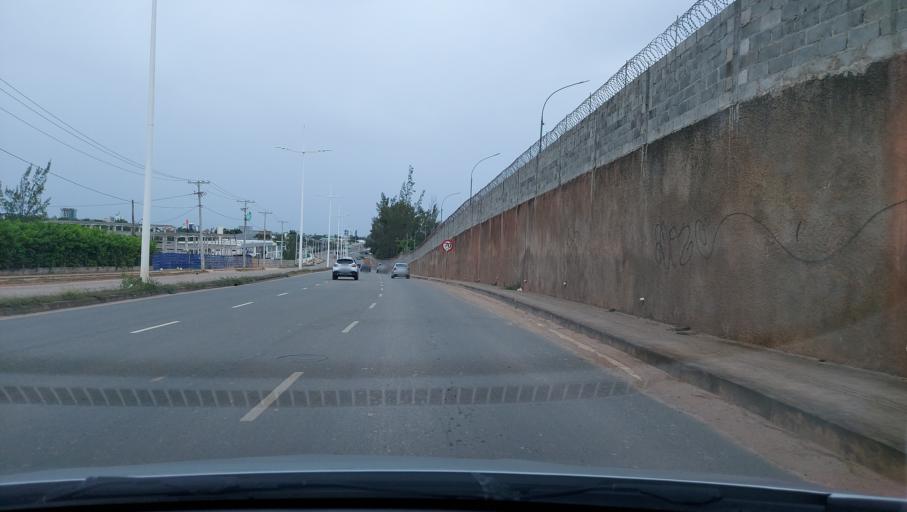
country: BR
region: Bahia
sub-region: Lauro De Freitas
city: Lauro de Freitas
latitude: -12.9410
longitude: -38.3864
